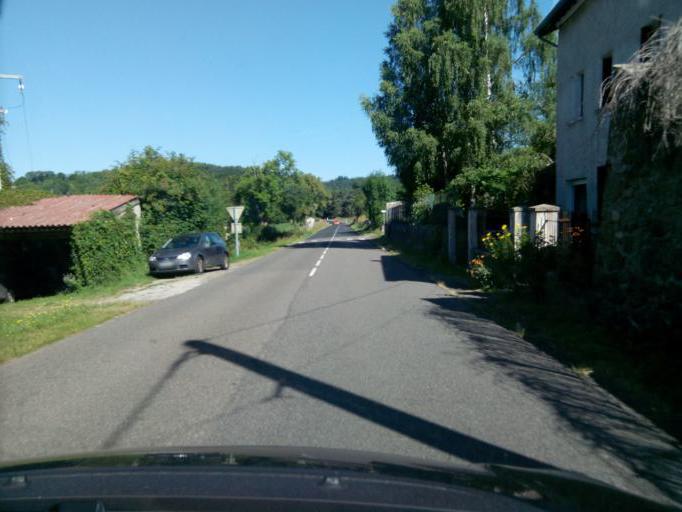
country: FR
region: Rhone-Alpes
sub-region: Departement de la Loire
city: Usson-en-Forez
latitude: 45.3814
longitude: 3.9956
